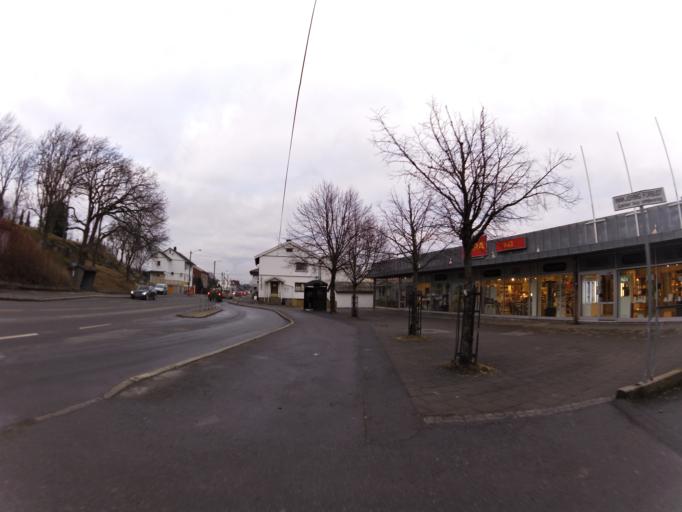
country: NO
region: Ostfold
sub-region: Fredrikstad
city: Fredrikstad
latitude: 59.2168
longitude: 10.9051
